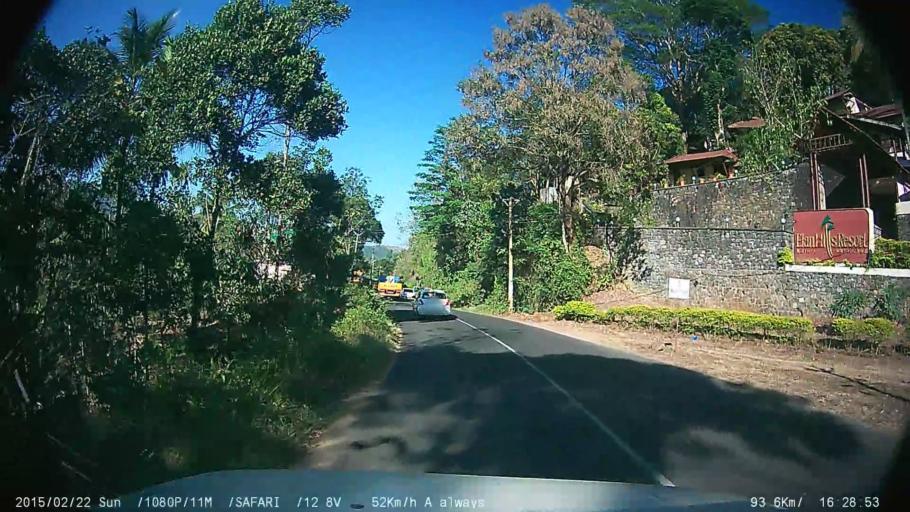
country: IN
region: Tamil Nadu
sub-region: Theni
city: Gudalur
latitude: 9.6115
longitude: 77.1503
